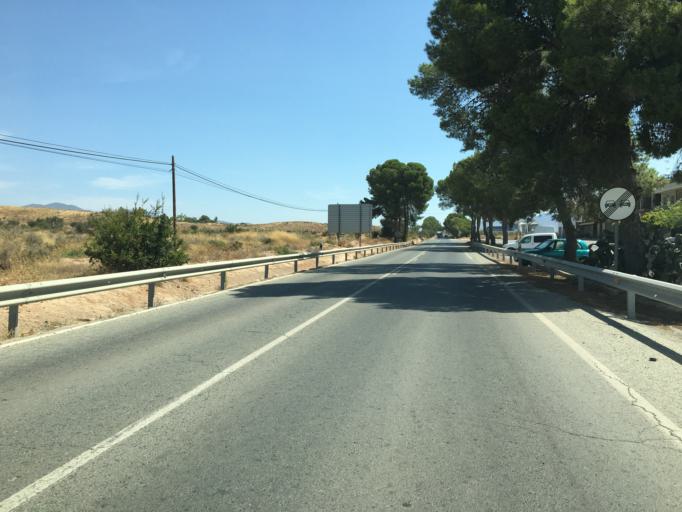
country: ES
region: Andalusia
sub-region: Provincia de Almeria
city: Huercal-Overa
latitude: 37.4106
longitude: -1.9309
